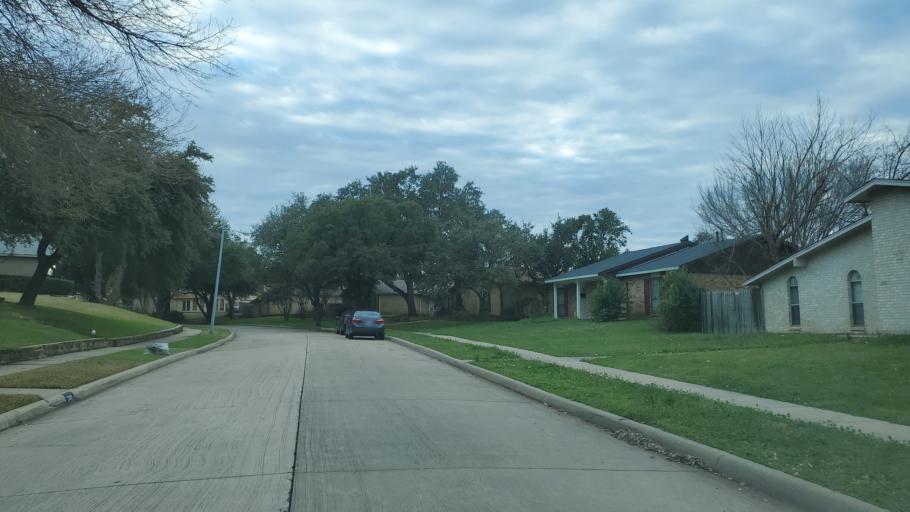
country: US
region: Texas
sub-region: Dallas County
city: Carrollton
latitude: 32.9939
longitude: -96.8878
